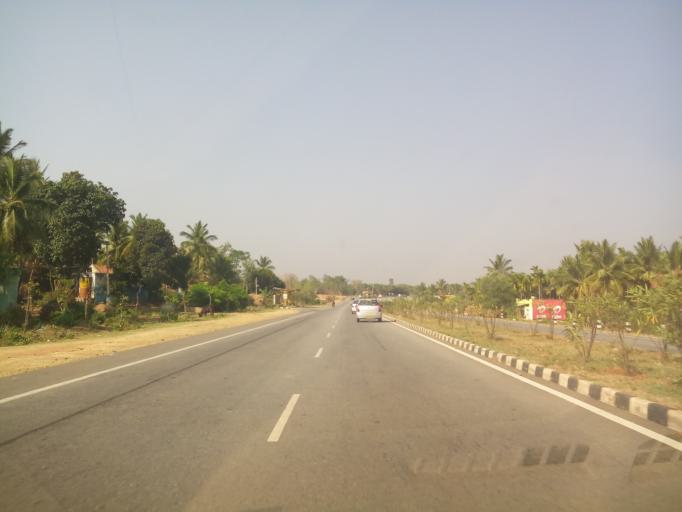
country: IN
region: Karnataka
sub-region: Ramanagara
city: Magadi
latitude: 13.0502
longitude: 77.1483
